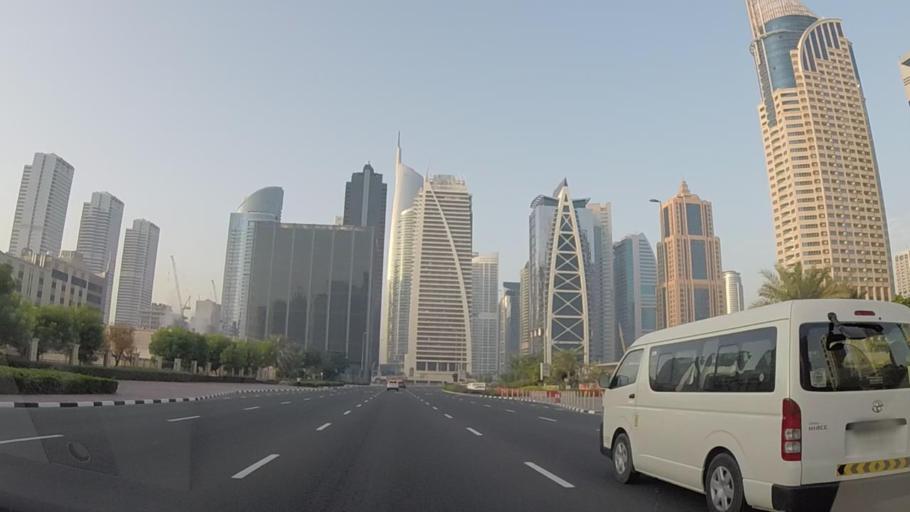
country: AE
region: Dubai
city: Dubai
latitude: 25.0743
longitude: 55.1465
